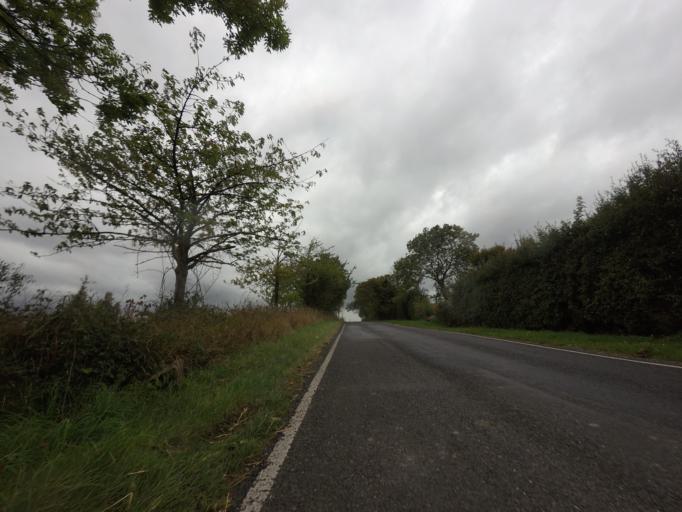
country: GB
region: England
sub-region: Cambridgeshire
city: Comberton
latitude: 52.1712
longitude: -0.0165
